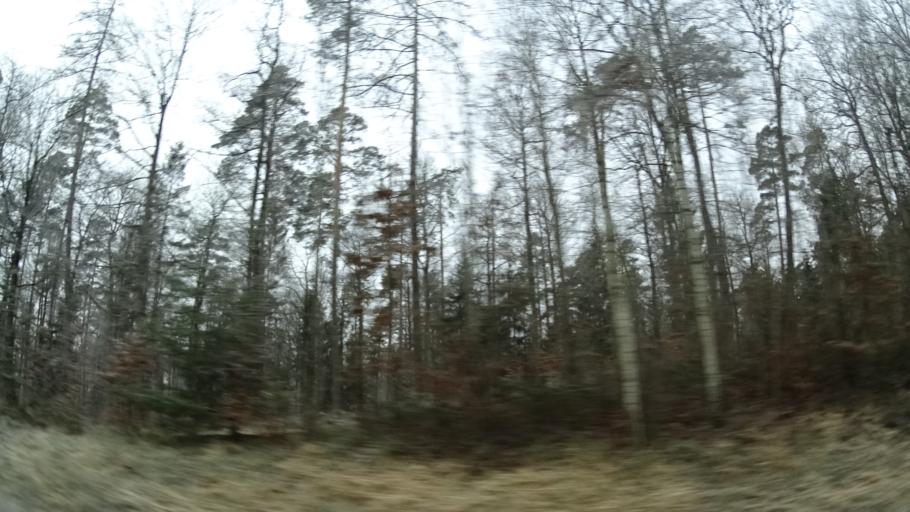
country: DE
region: Bavaria
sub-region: Regierungsbezirk Unterfranken
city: Maroldsweisach
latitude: 50.1683
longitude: 10.6886
